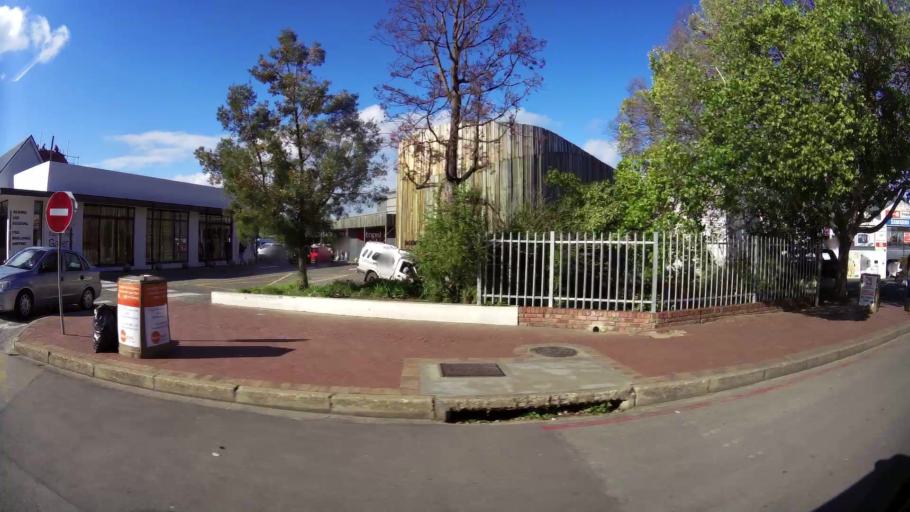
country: ZA
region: Western Cape
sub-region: Eden District Municipality
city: Knysna
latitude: -34.0349
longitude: 23.0435
